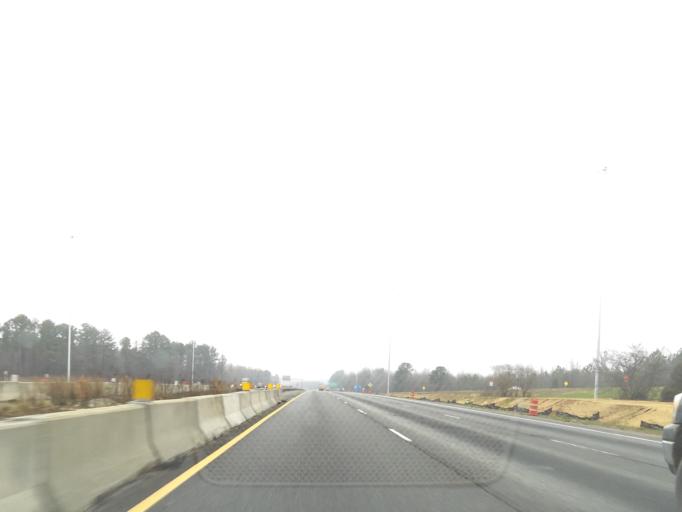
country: US
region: Georgia
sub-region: Henry County
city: Stockbridge
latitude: 33.4825
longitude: -84.2172
